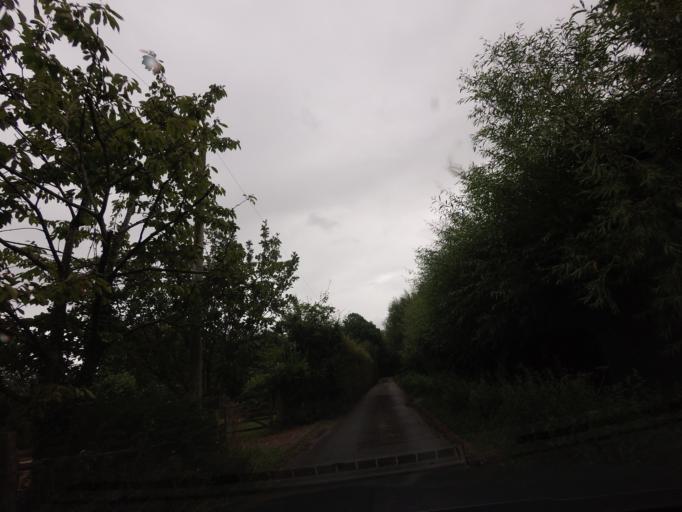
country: GB
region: England
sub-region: Kent
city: Paddock Wood
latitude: 51.1895
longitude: 0.4136
